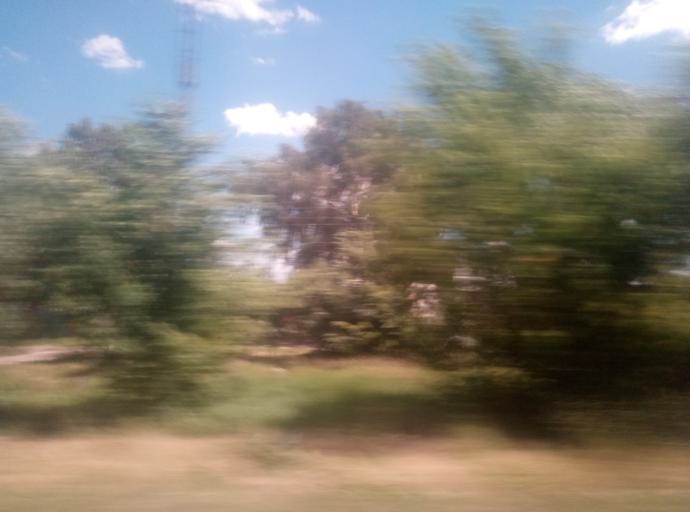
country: RU
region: Tula
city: Kireyevsk
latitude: 53.9645
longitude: 37.9365
